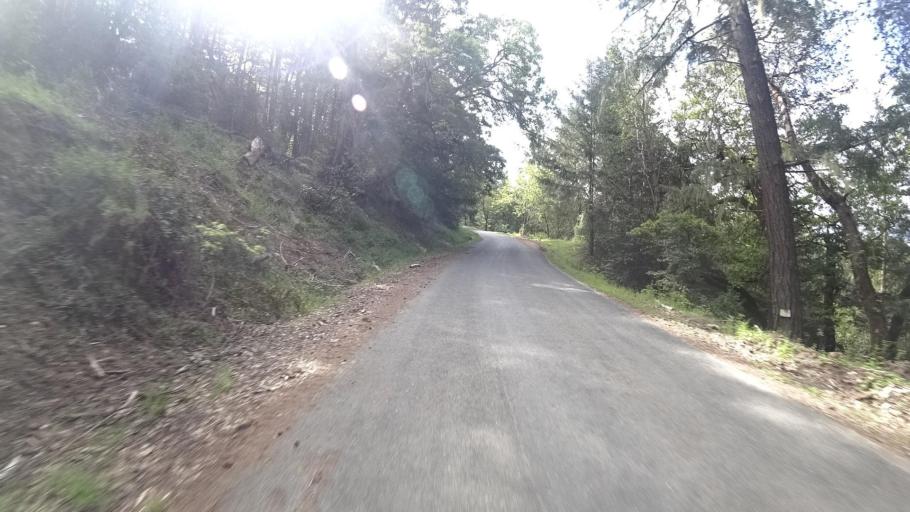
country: US
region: California
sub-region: Humboldt County
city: Redway
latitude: 40.1697
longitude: -123.5646
